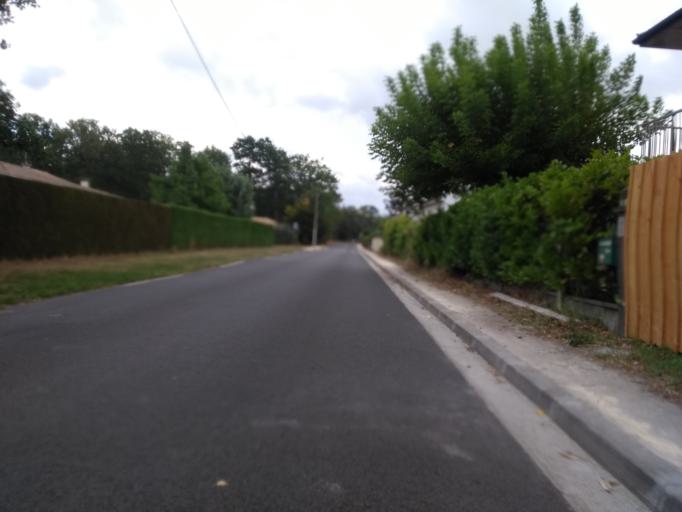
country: FR
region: Aquitaine
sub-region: Departement de la Gironde
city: Pessac
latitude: 44.8116
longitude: -0.6559
